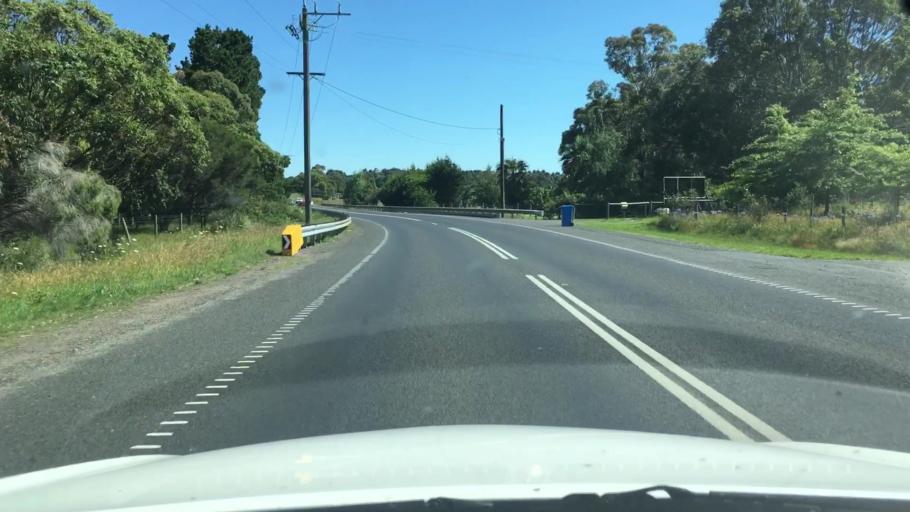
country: AU
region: Victoria
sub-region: Casey
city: Narre Warren North
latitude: -37.9710
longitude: 145.3162
